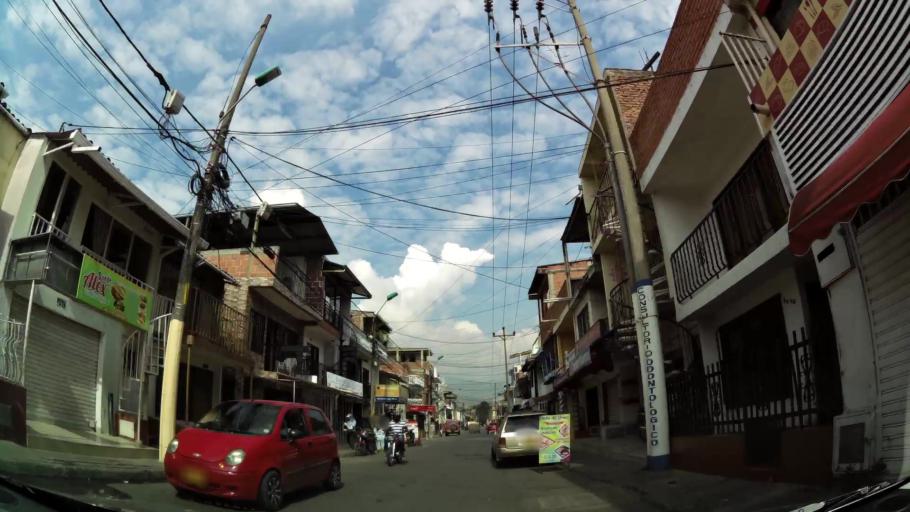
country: CO
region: Valle del Cauca
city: Cali
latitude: 3.4958
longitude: -76.4941
